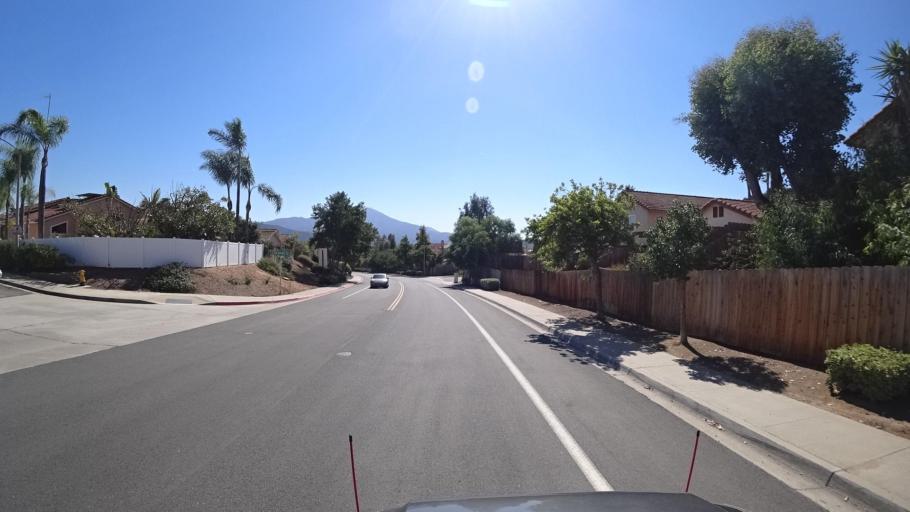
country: US
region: California
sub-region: San Diego County
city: Rancho San Diego
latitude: 32.7529
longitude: -116.9352
